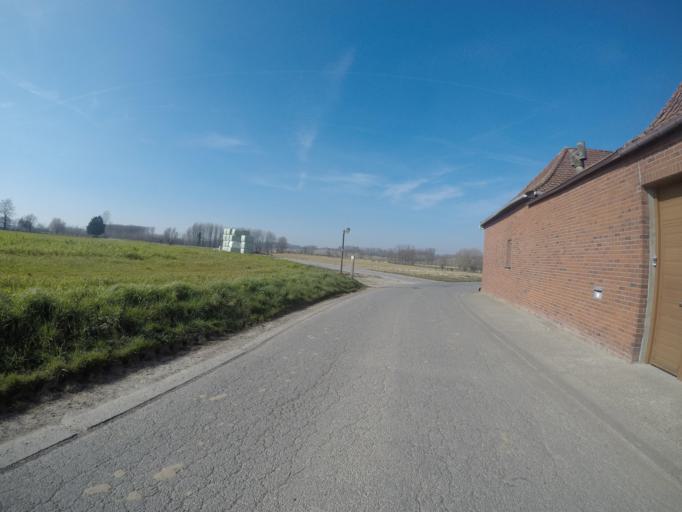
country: BE
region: Flanders
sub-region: Provincie Oost-Vlaanderen
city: Sint-Maria-Lierde
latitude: 50.7904
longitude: 3.8223
